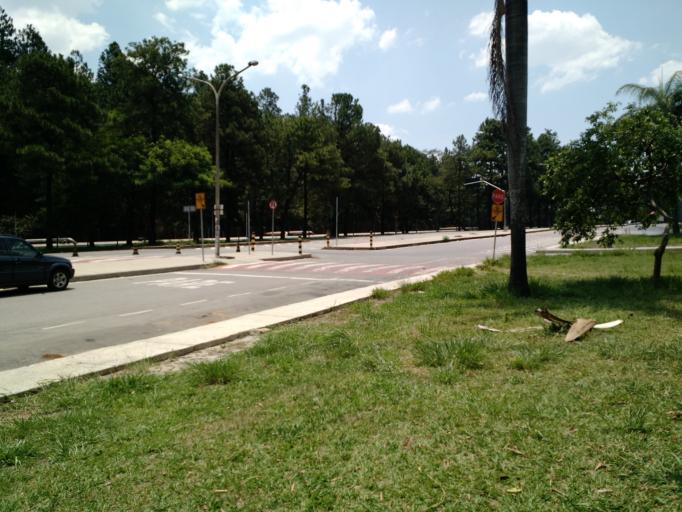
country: BR
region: Minas Gerais
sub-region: Contagem
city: Contagem
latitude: -19.9629
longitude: -44.0944
